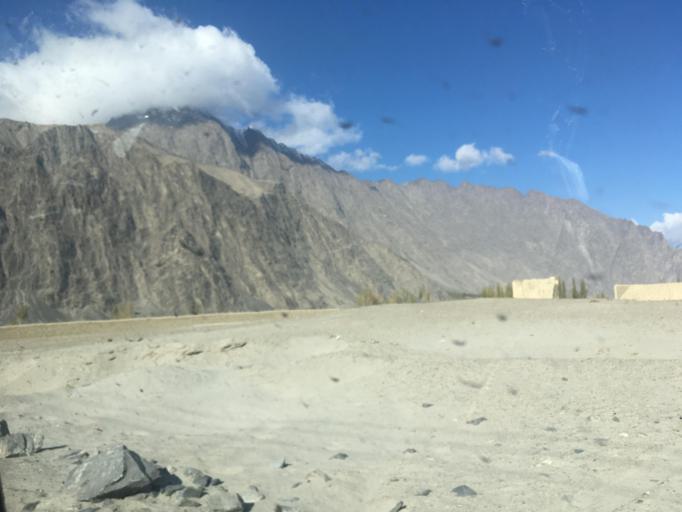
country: PK
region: Gilgit-Baltistan
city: Skardu
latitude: 35.3550
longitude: 75.5222
